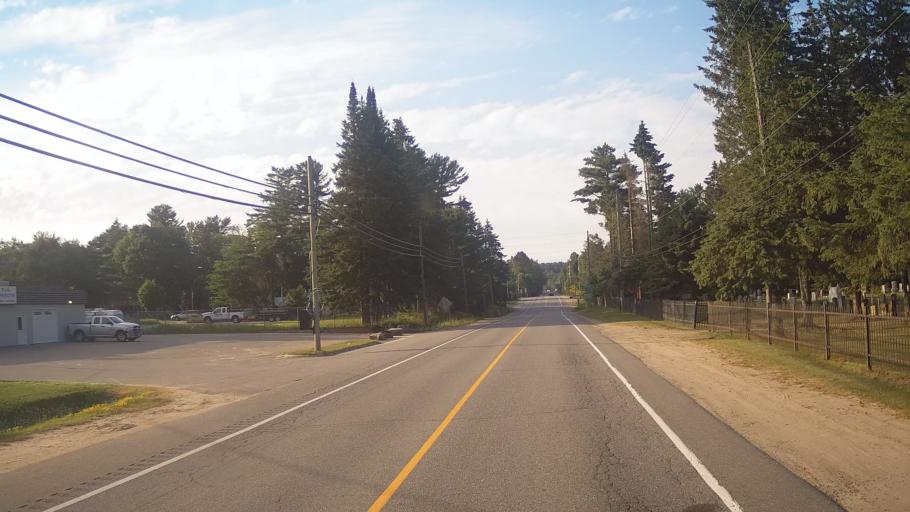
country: CA
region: Ontario
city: Huntsville
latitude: 45.3434
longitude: -79.2013
